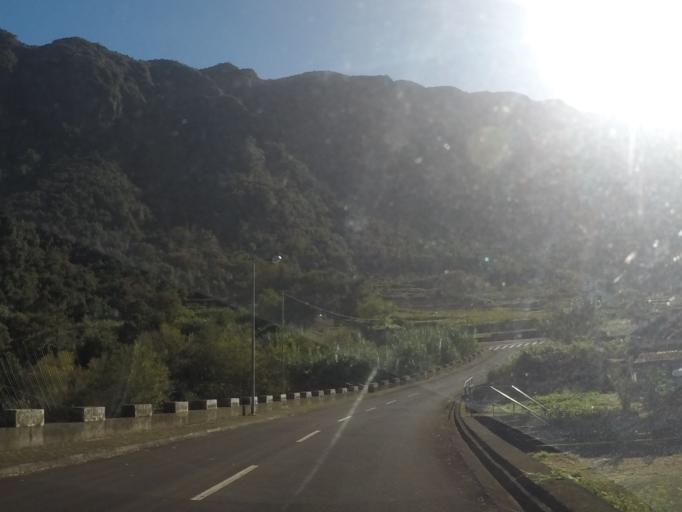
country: PT
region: Madeira
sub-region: Santana
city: Santana
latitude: 32.8025
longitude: -16.9603
